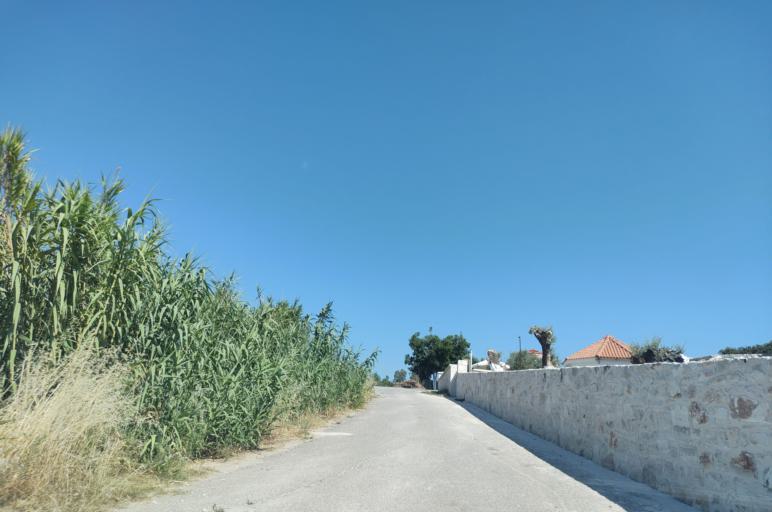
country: GR
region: Crete
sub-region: Nomos Chanias
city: Georgioupolis
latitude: 35.3610
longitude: 24.2484
